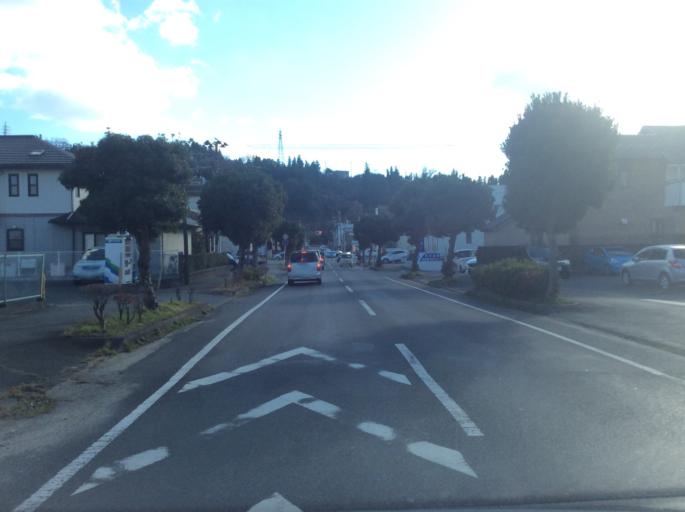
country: JP
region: Fukushima
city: Iwaki
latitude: 37.0489
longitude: 140.8848
